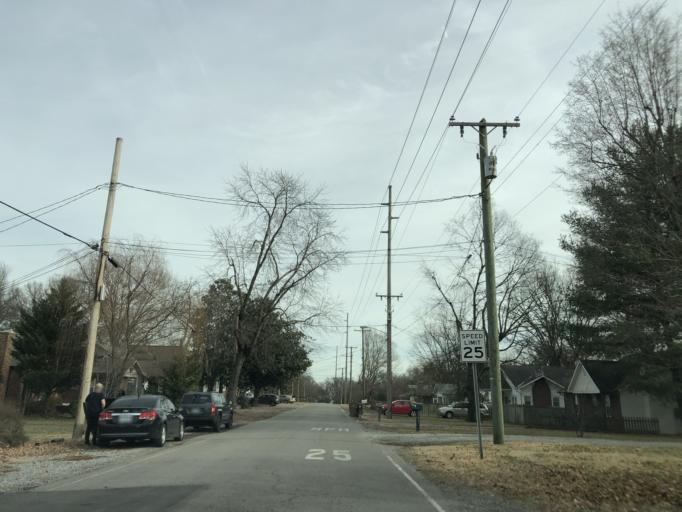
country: US
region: Tennessee
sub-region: Davidson County
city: Nashville
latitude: 36.2116
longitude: -86.7281
